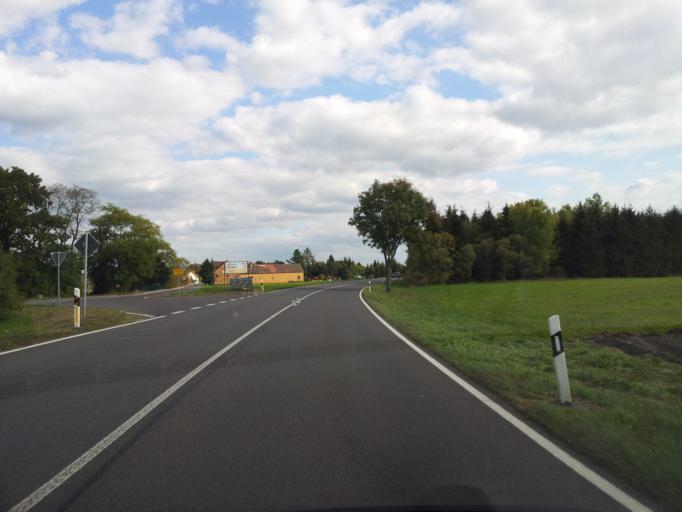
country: DE
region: Brandenburg
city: Sallgast
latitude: 51.6046
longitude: 13.8950
